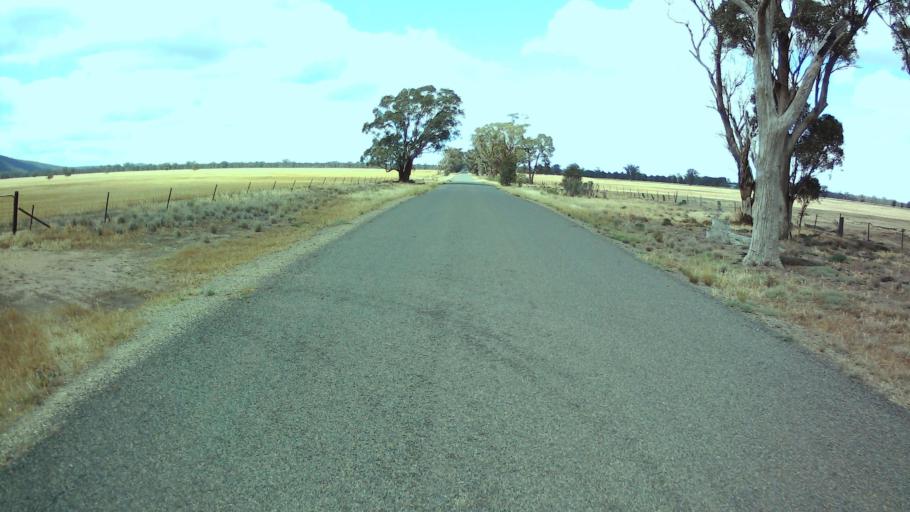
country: AU
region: New South Wales
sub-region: Weddin
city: Grenfell
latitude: -33.8813
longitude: 147.9244
